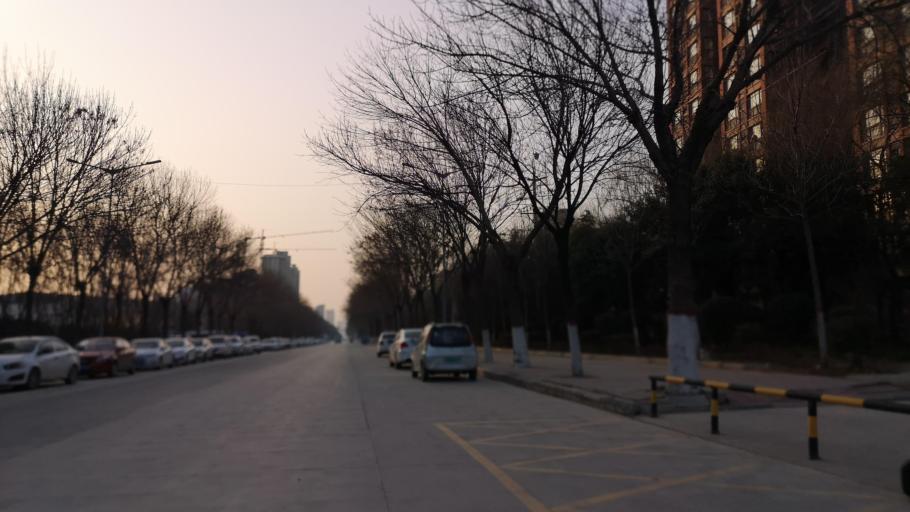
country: CN
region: Henan Sheng
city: Puyang Chengguanzhen
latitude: 35.7236
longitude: 115.0543
